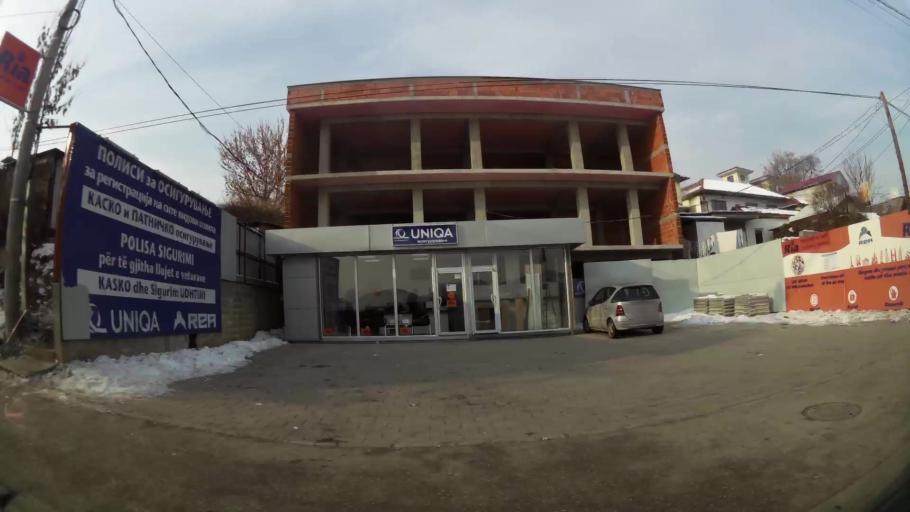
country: MK
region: Cair
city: Cair
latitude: 42.0136
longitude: 21.4314
